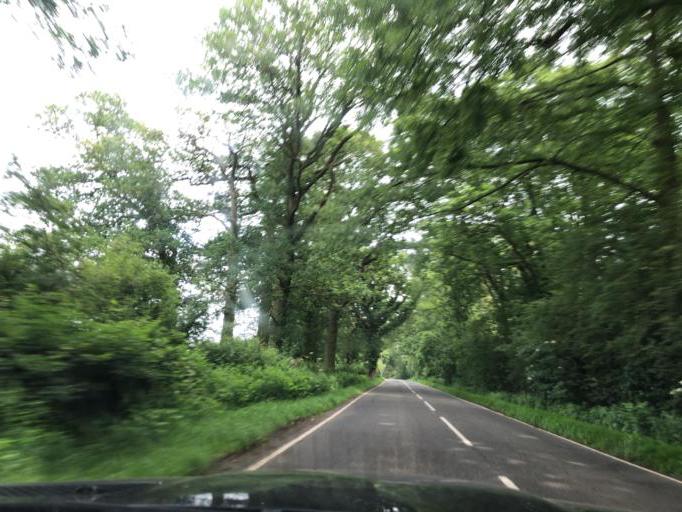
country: GB
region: England
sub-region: Warwickshire
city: Kenilworth
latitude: 52.3247
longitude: -1.6024
